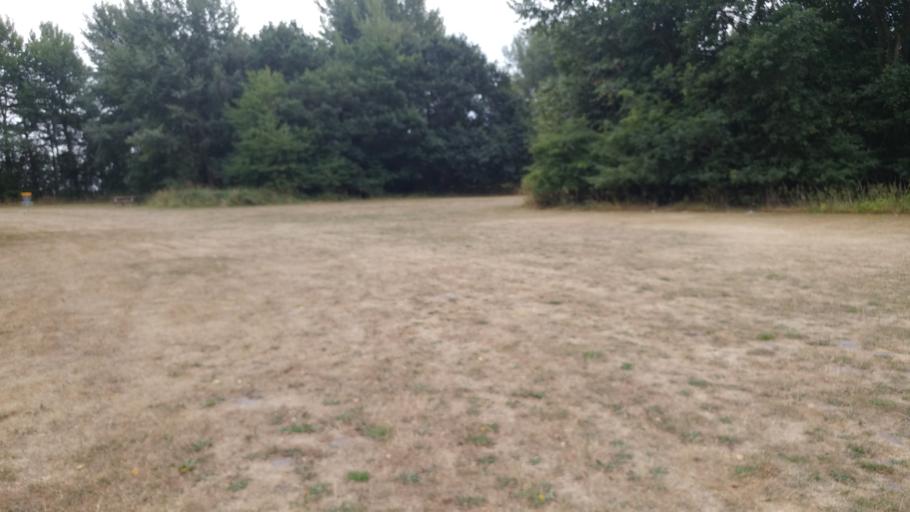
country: DK
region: South Denmark
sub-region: Nordfyns Kommune
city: Otterup
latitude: 55.5903
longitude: 10.4049
